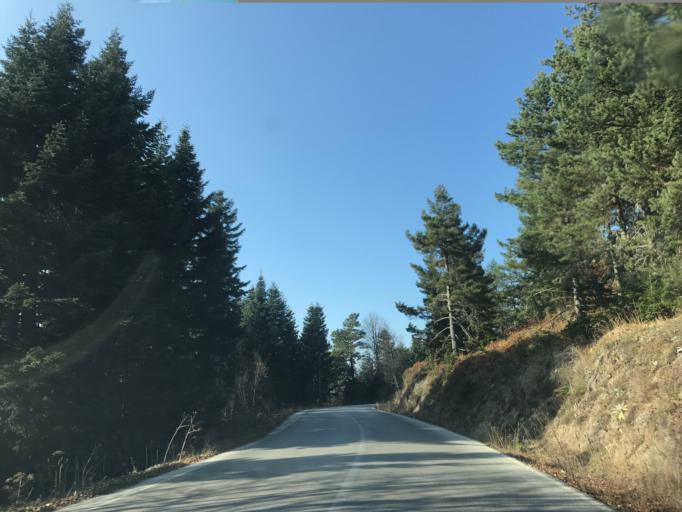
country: TR
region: Bolu
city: Bolu
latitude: 40.8889
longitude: 31.6774
